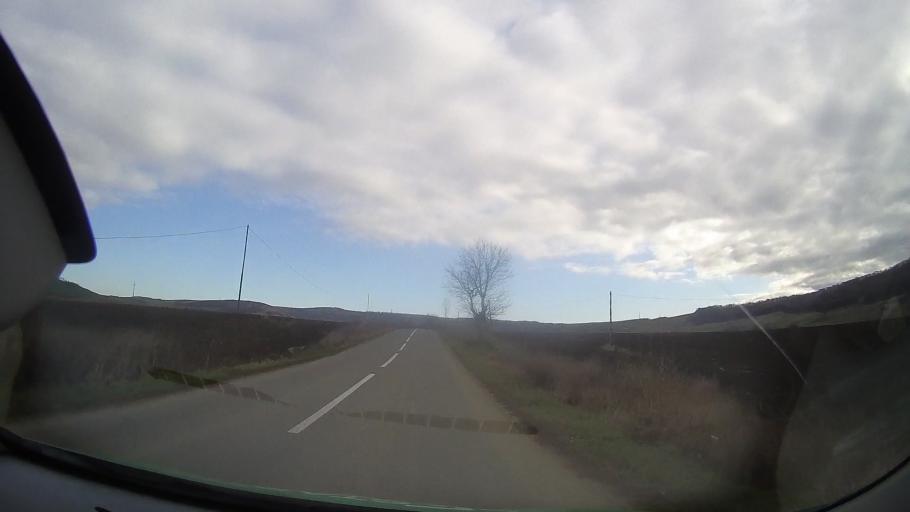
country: RO
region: Mures
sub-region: Comuna Iernut
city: Iernut
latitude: 46.4880
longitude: 24.2412
